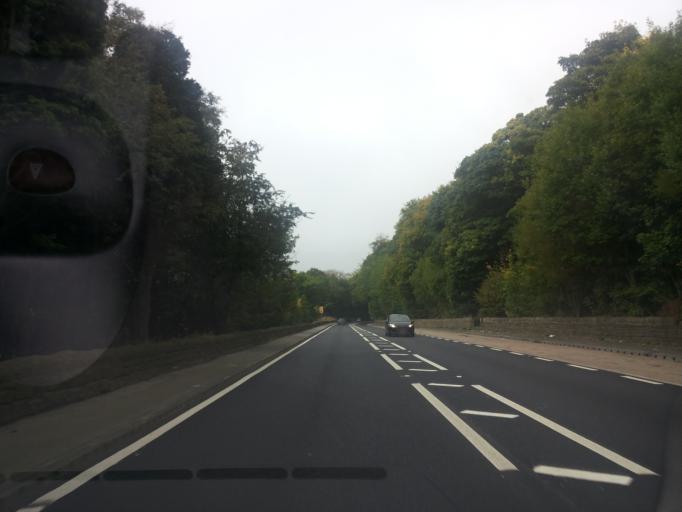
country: GB
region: England
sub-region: Barnsley
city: Penistone
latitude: 53.4922
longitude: -1.6303
